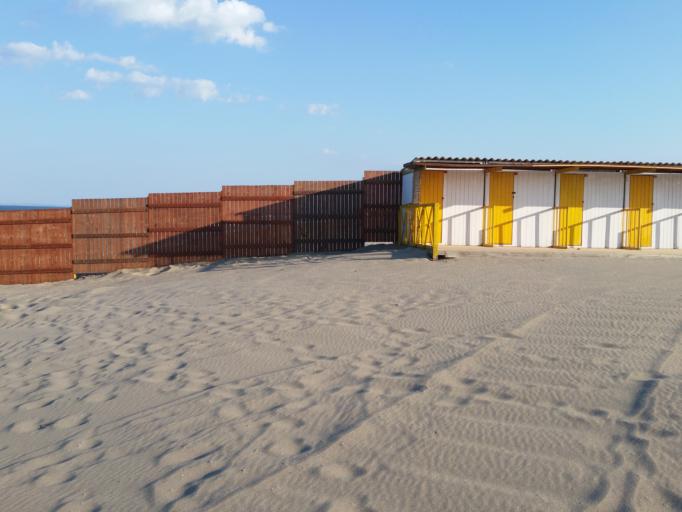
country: IT
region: Sicily
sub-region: Catania
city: Catania
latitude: 37.4483
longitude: 15.0868
